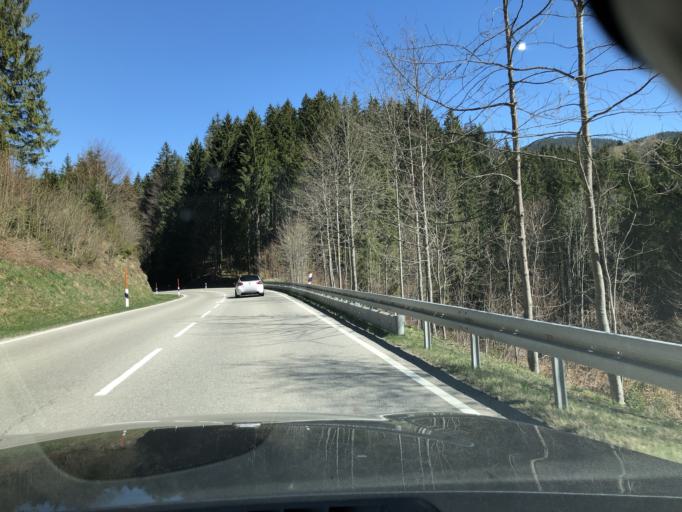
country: AT
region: Tyrol
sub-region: Politischer Bezirk Reutte
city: Jungholz
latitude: 47.5718
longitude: 10.4308
